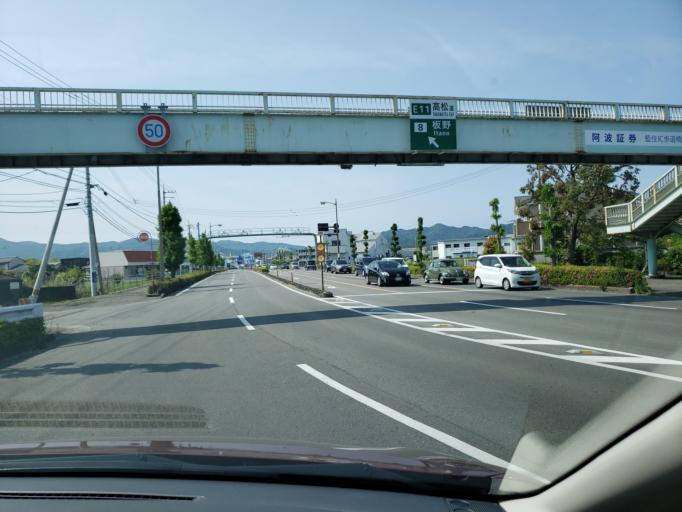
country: JP
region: Tokushima
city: Ishii
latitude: 34.1204
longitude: 134.4798
